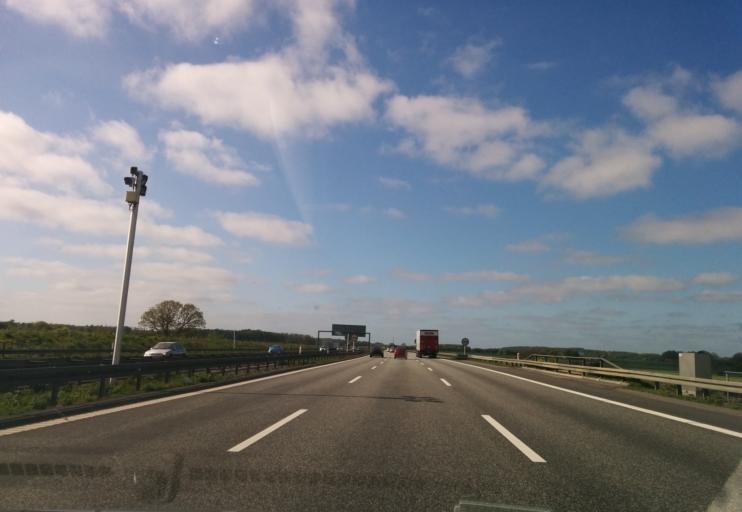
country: DK
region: South Denmark
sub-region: Vejle Kommune
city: Borkop
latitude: 55.6148
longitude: 9.5800
